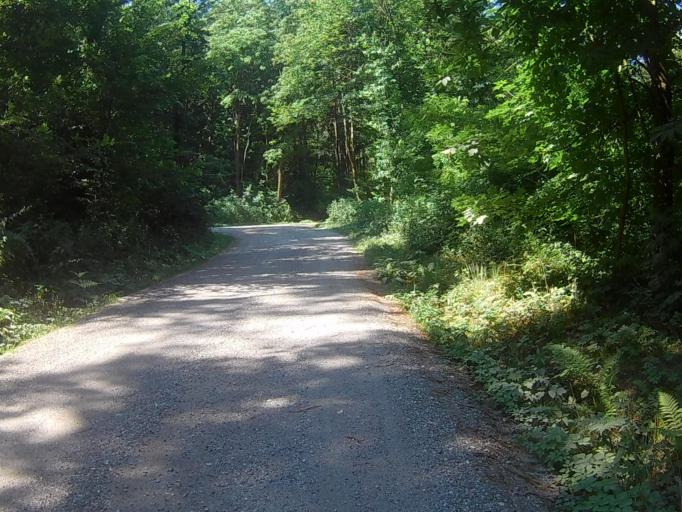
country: SI
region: Hoce-Slivnica
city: Radizel
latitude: 46.4813
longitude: 15.6400
